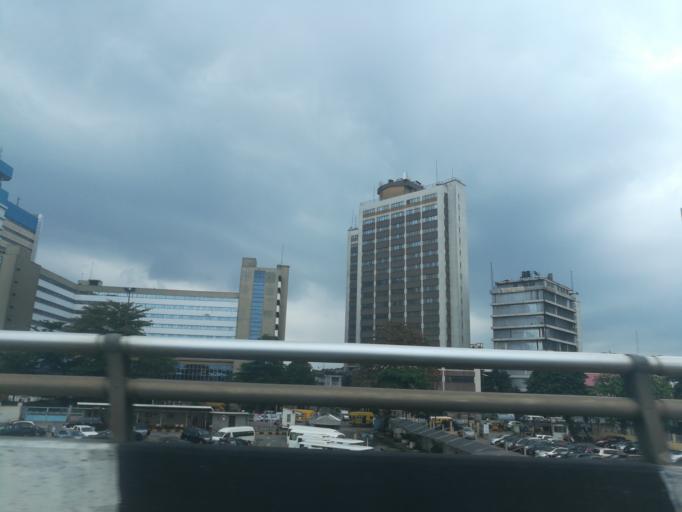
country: NG
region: Lagos
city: Lagos
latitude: 6.4484
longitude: 3.3923
